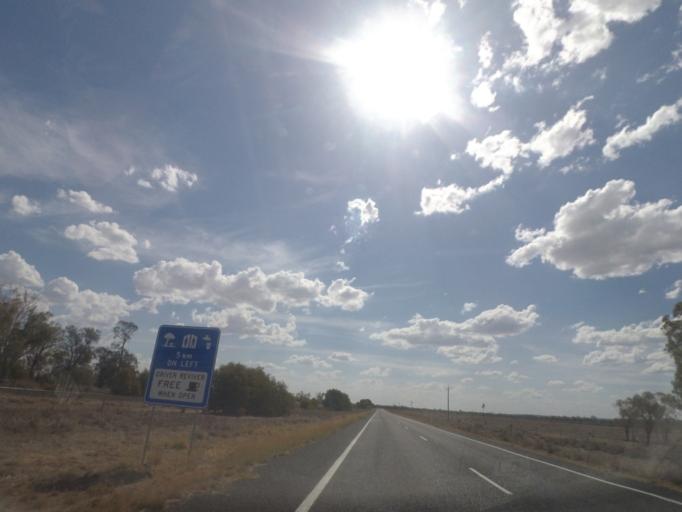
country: AU
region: New South Wales
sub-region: Moree Plains
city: Boggabilla
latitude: -28.4147
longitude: 151.1371
